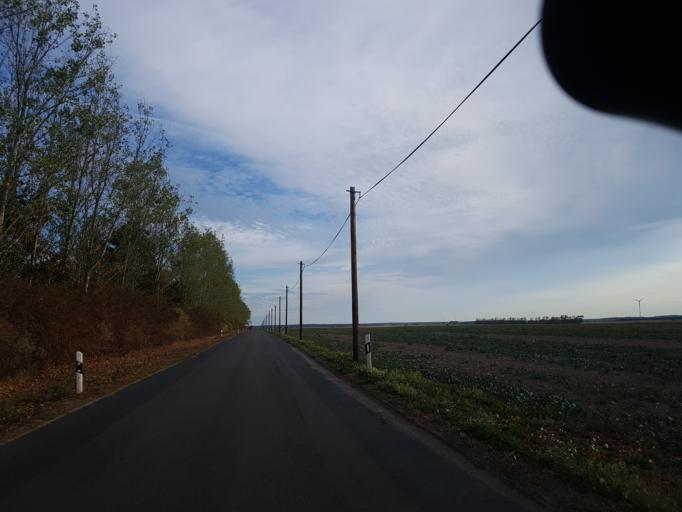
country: DE
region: Brandenburg
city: Dahme
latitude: 51.8659
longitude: 13.3833
